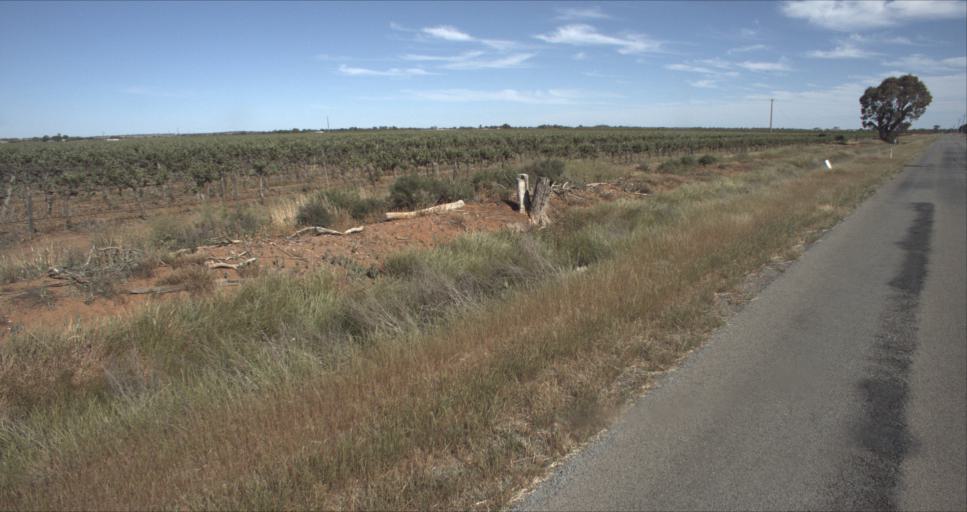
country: AU
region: New South Wales
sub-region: Leeton
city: Leeton
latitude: -34.5770
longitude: 146.3806
